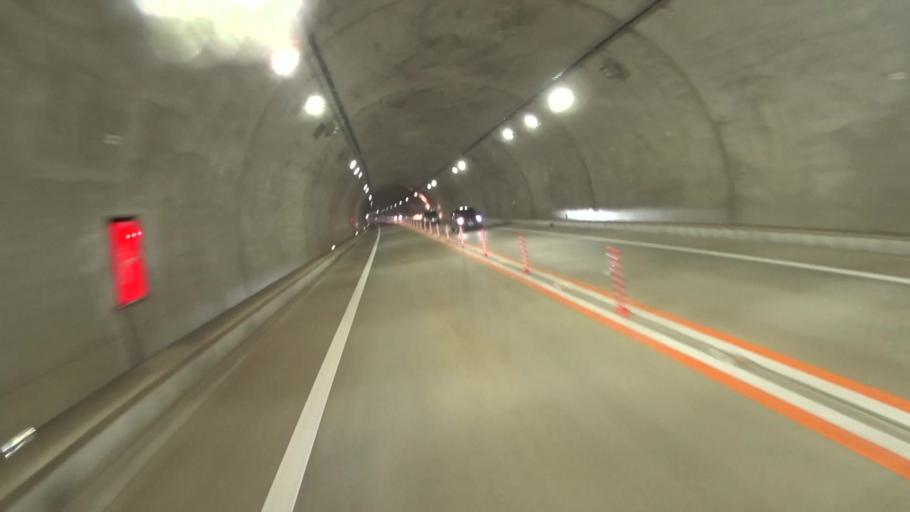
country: JP
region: Kyoto
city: Ayabe
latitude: 35.2097
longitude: 135.3459
